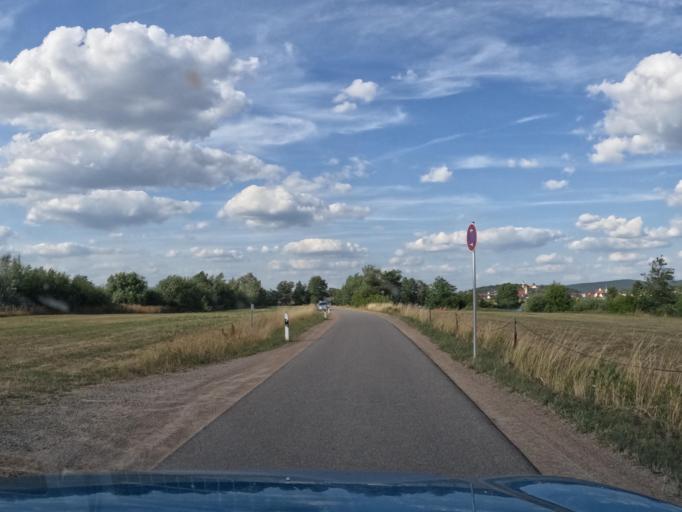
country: DE
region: Bavaria
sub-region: Upper Palatinate
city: Schwarzenfeld
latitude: 49.3775
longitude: 12.1198
